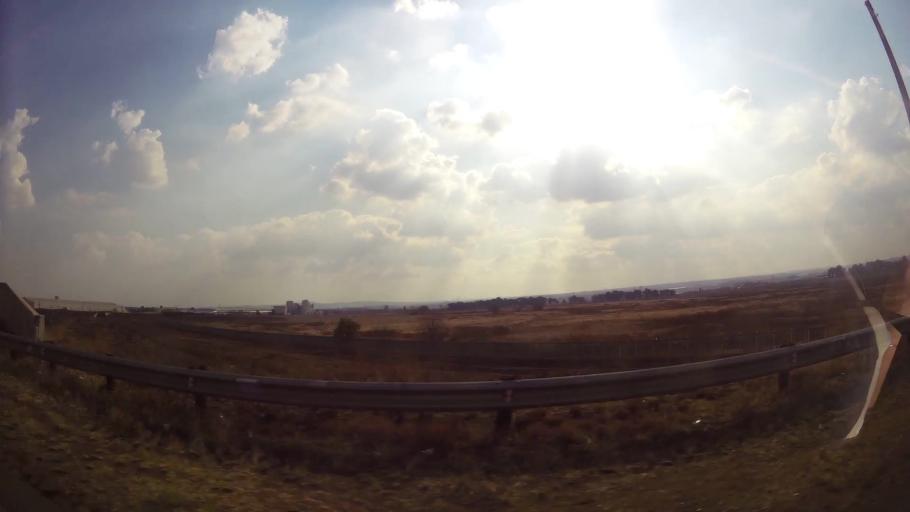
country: ZA
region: Gauteng
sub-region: Ekurhuleni Metropolitan Municipality
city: Germiston
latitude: -26.3039
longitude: 28.2103
